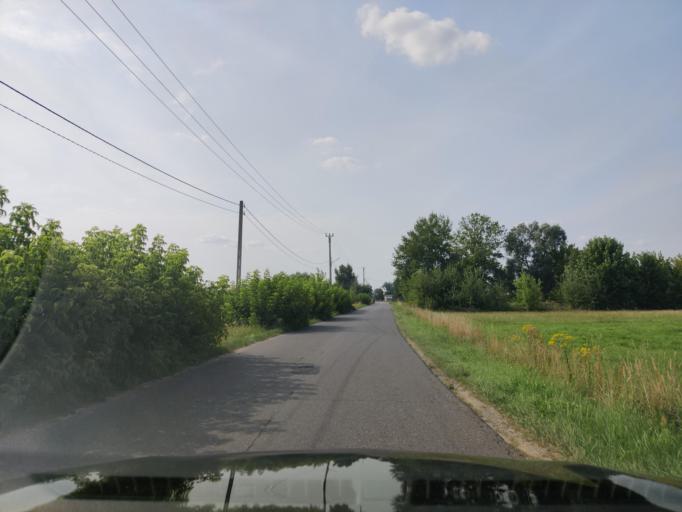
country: PL
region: Masovian Voivodeship
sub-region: Powiat wyszkowski
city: Rzasnik
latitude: 52.7380
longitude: 21.3437
